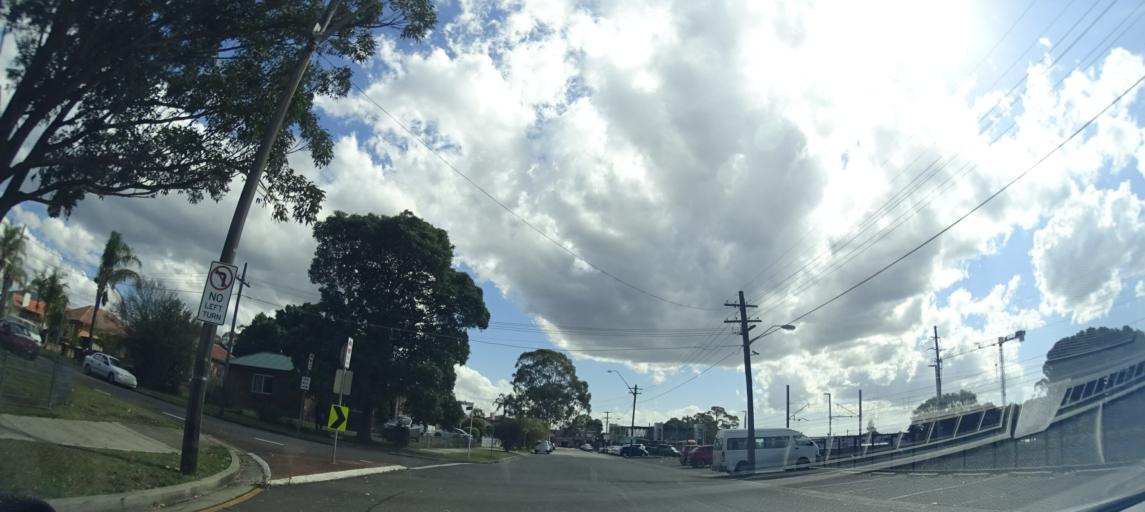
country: AU
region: New South Wales
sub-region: Bankstown
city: Revesby
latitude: -33.9543
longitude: 151.0003
